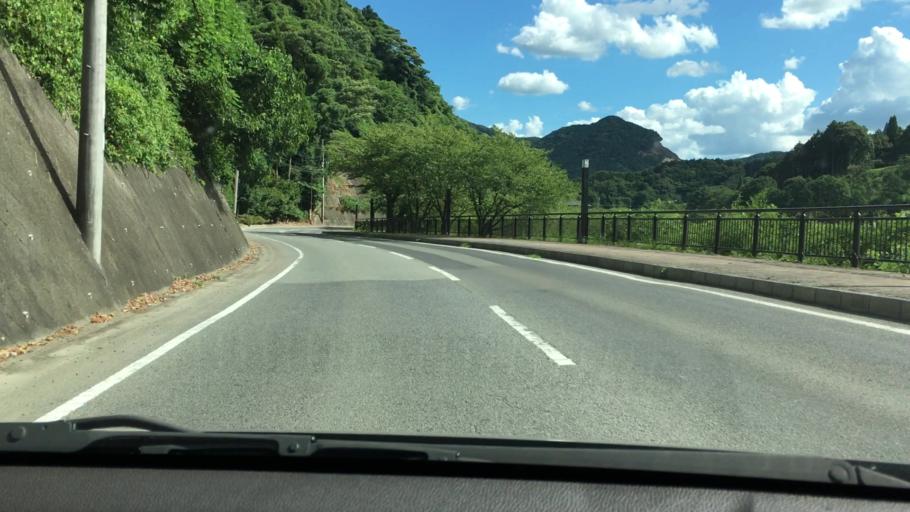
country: JP
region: Saga Prefecture
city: Takeocho-takeo
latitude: 33.1820
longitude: 130.0376
